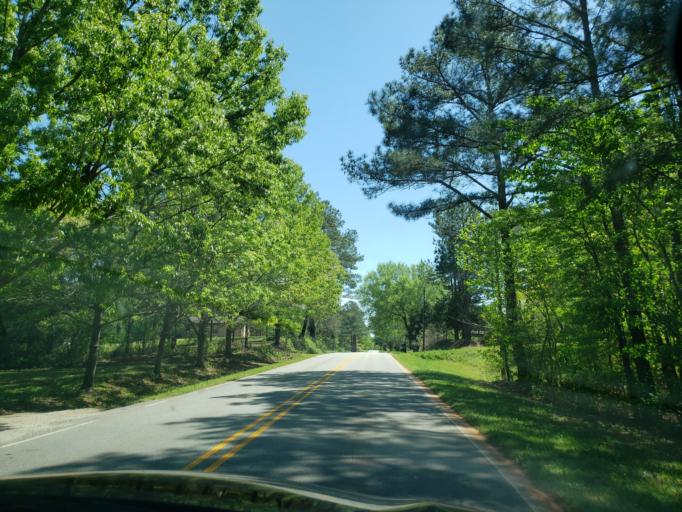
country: US
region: Alabama
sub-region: Tallapoosa County
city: Camp Hill
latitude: 32.6994
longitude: -85.6851
